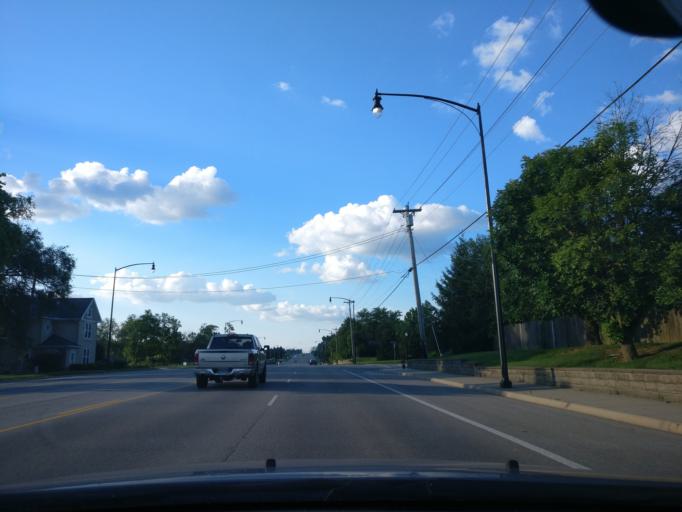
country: US
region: Ohio
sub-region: Warren County
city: Springboro
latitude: 39.5653
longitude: -84.2320
